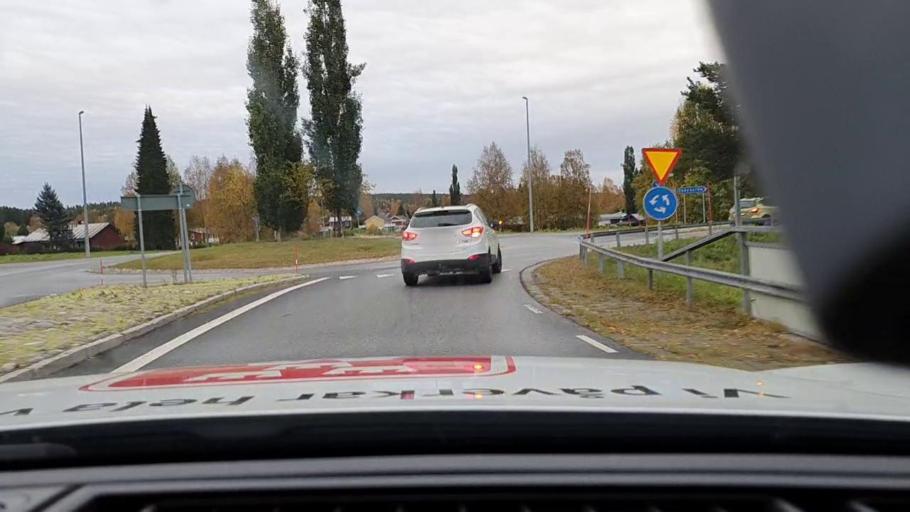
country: SE
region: Norrbotten
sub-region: Bodens Kommun
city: Saevast
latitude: 65.7683
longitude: 21.7394
